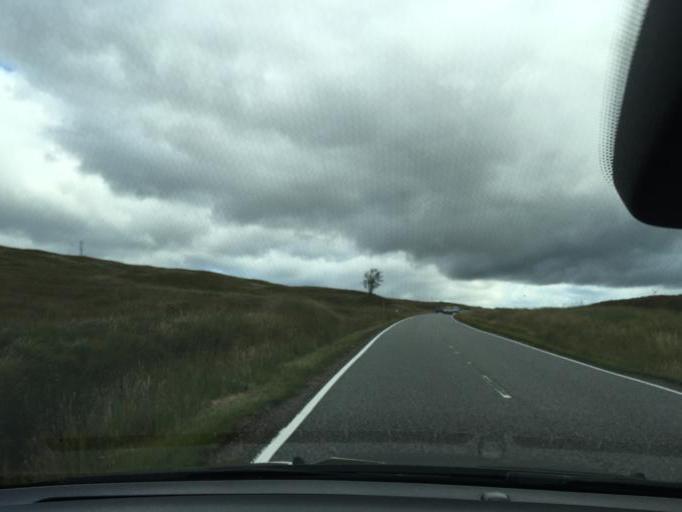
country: GB
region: Scotland
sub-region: Highland
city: Spean Bridge
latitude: 56.5796
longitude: -4.7553
